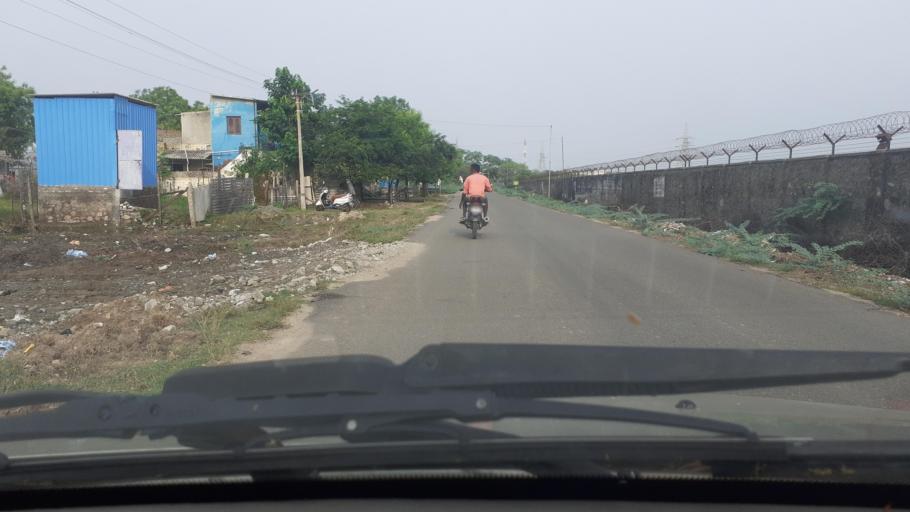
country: IN
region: Tamil Nadu
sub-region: Thoothukkudi
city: Korampallam
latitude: 8.7944
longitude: 78.1063
